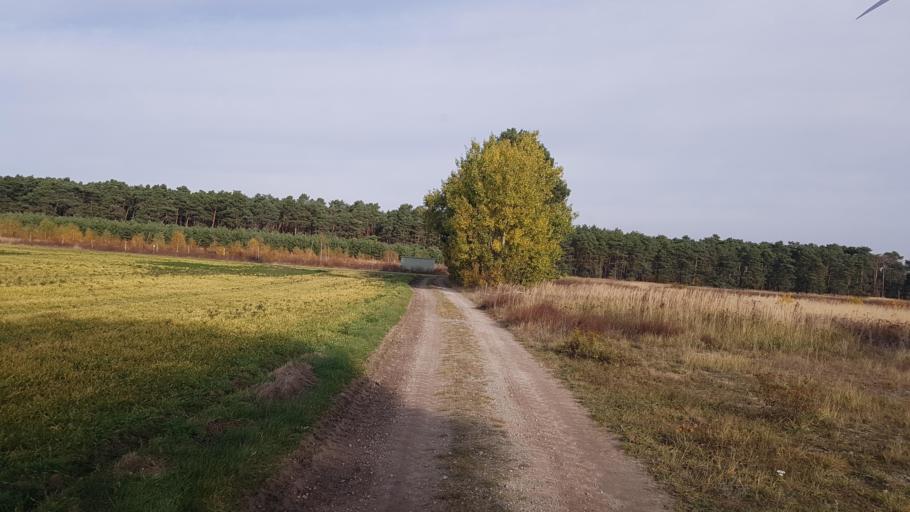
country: DE
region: Brandenburg
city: Treuenbrietzen
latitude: 52.0163
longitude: 12.8873
